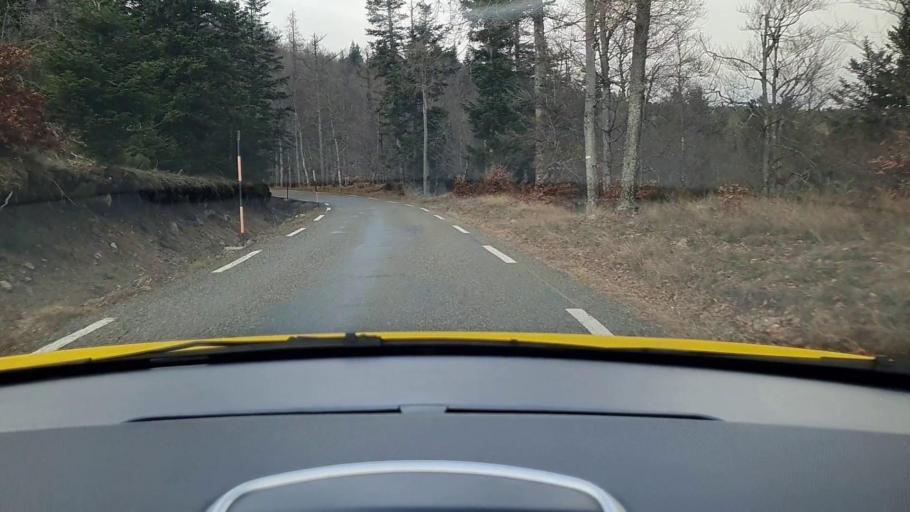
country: FR
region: Languedoc-Roussillon
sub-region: Departement du Gard
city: Branoux-les-Taillades
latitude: 44.3725
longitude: 3.9138
